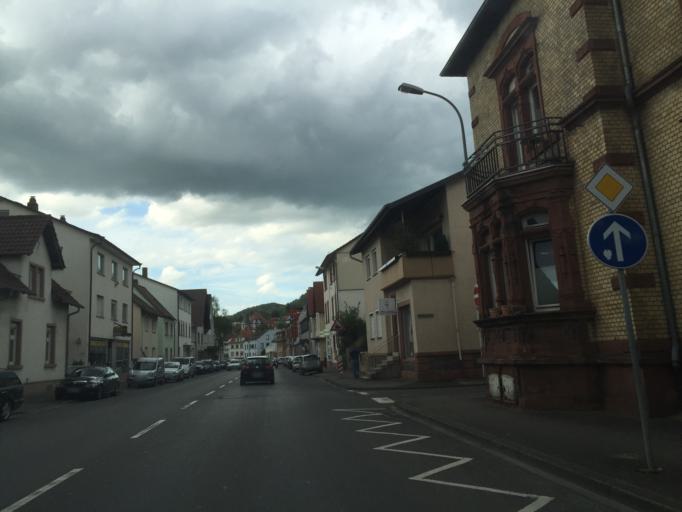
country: DE
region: Baden-Wuerttemberg
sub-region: Karlsruhe Region
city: Weinheim
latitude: 49.5564
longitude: 8.6699
